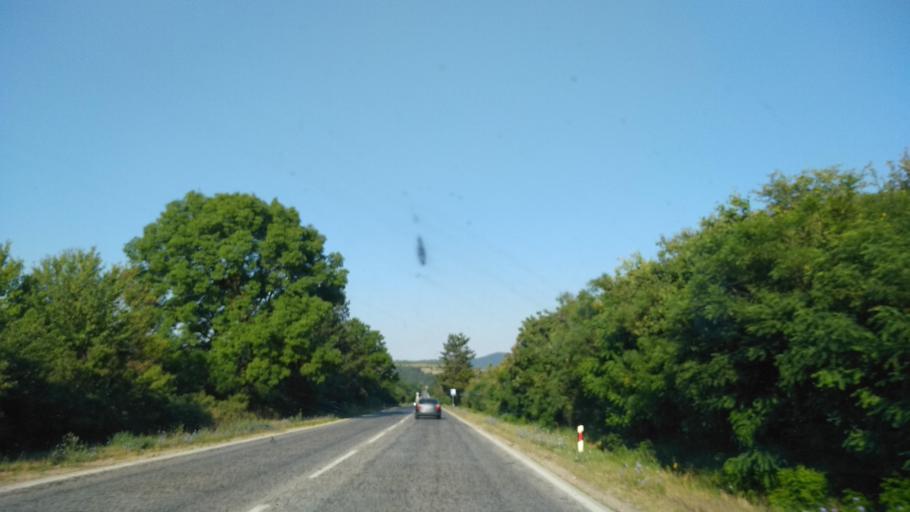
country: BG
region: Lovech
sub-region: Obshtina Lovech
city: Lovech
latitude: 43.0500
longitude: 24.8967
